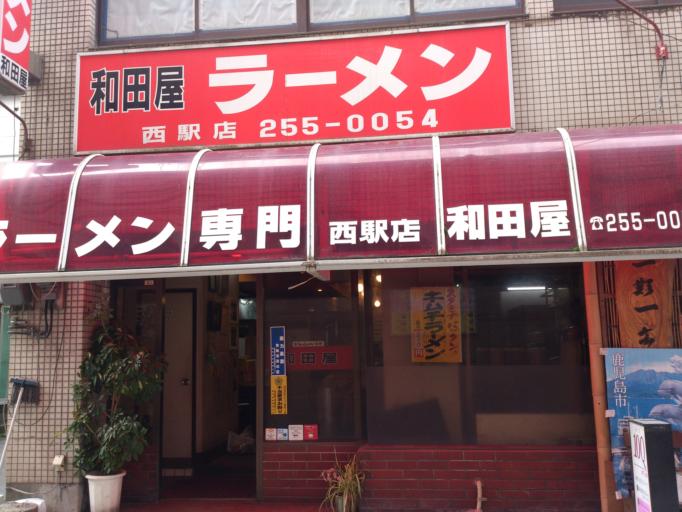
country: JP
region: Kagoshima
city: Kagoshima-shi
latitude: 31.5859
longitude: 130.5435
